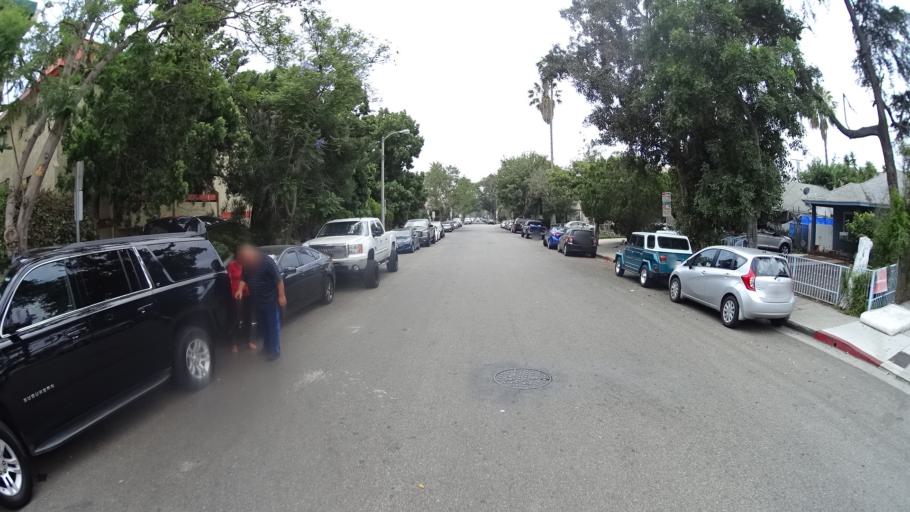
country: US
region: California
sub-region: Los Angeles County
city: West Hollywood
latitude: 34.0881
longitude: -118.3605
